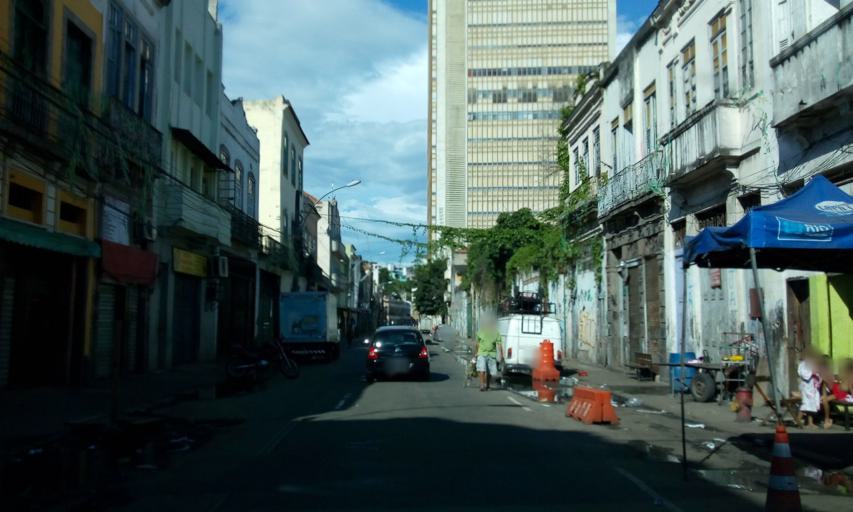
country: BR
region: Rio de Janeiro
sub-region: Rio De Janeiro
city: Rio de Janeiro
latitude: -22.9014
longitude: -43.1896
